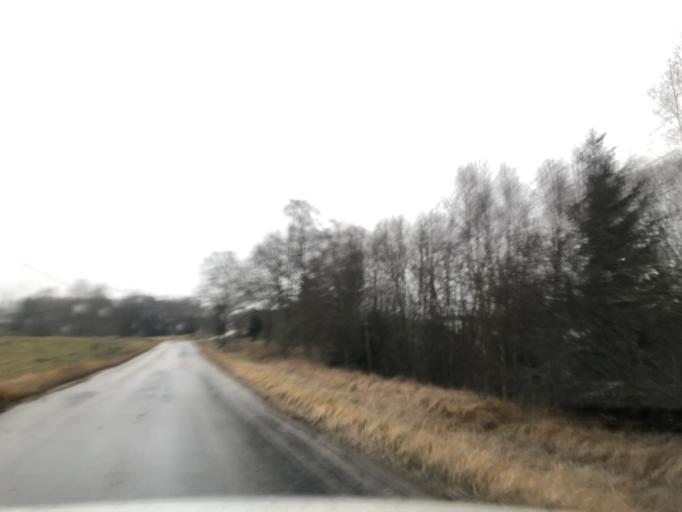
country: SE
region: Vaestra Goetaland
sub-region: Ulricehamns Kommun
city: Ulricehamn
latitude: 57.8536
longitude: 13.5477
